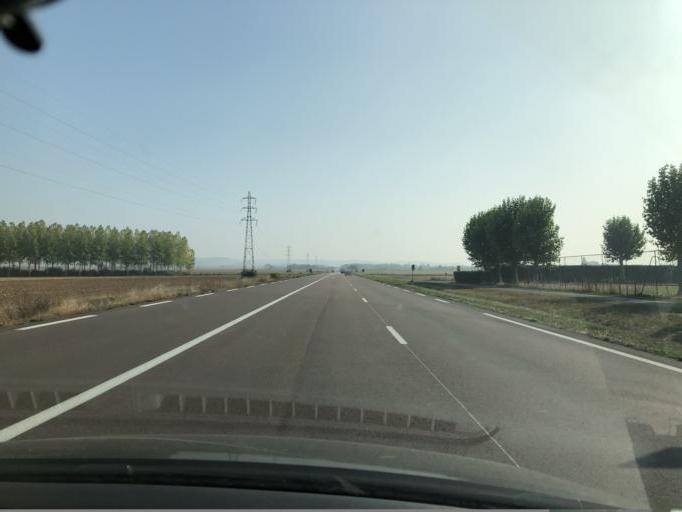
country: FR
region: Bourgogne
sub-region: Departement de l'Yonne
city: Saint-Martin-du-Tertre
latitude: 48.2301
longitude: 3.2709
